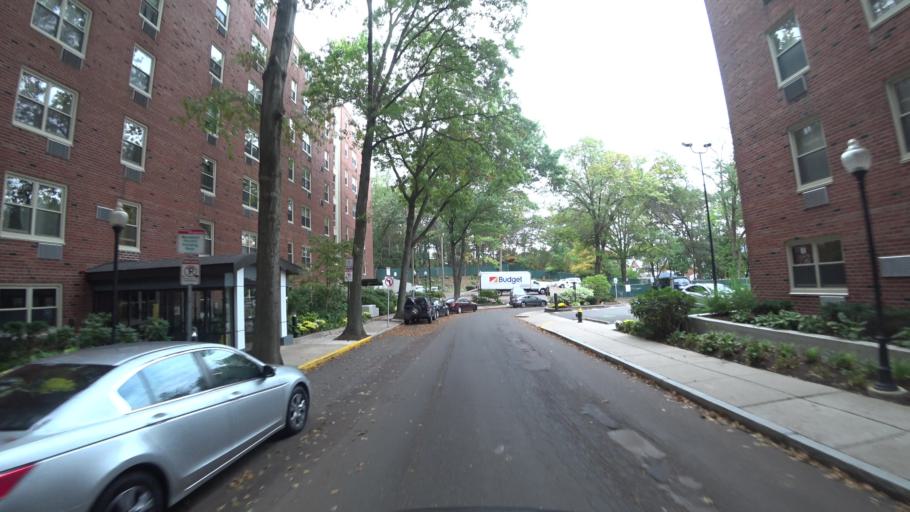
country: US
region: Massachusetts
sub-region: Norfolk County
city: Brookline
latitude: 42.3499
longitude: -71.1411
